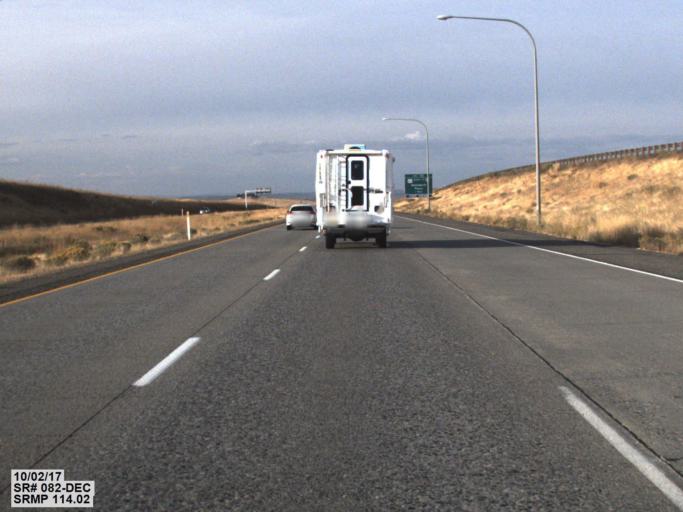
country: US
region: Washington
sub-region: Benton County
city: Highland
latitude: 46.1479
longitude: -119.2018
